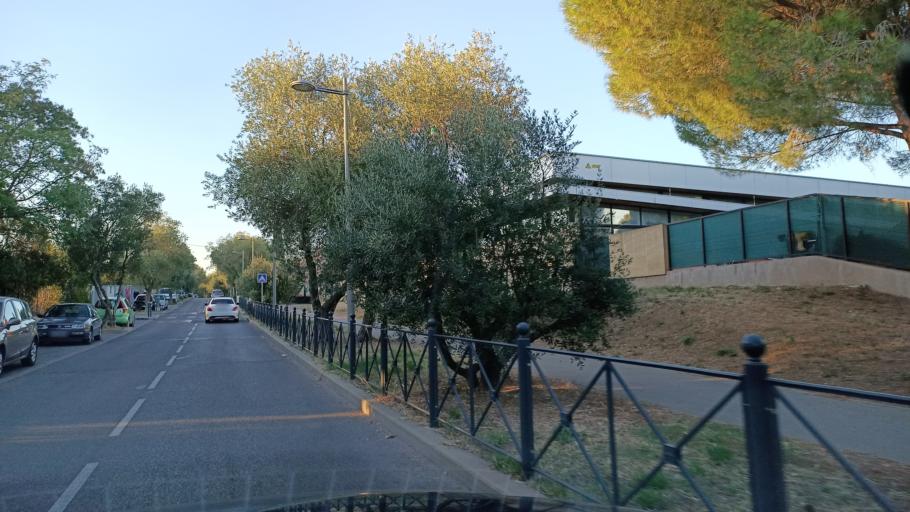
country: FR
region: Languedoc-Roussillon
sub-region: Departement de l'Herault
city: Saint-Jean-de-Vedas
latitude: 43.5845
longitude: 3.8560
